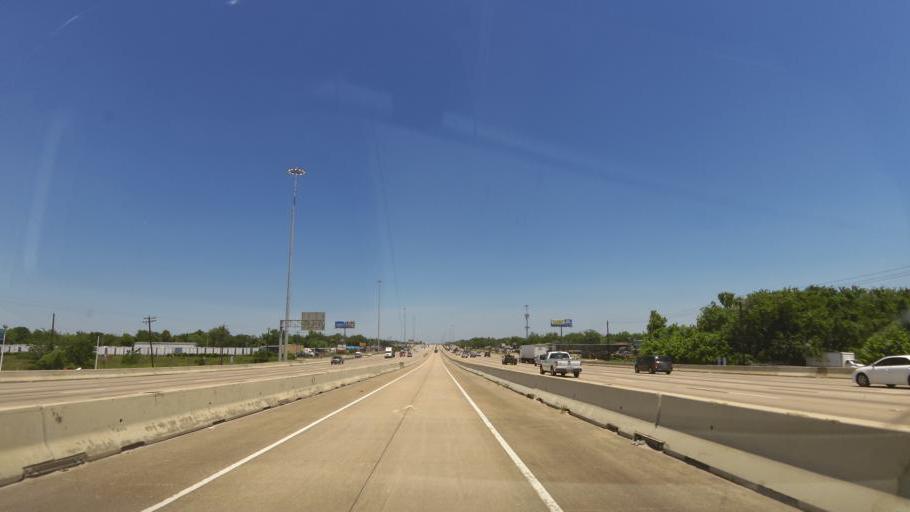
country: US
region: Texas
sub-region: Harris County
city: Aldine
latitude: 29.8722
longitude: -95.3289
